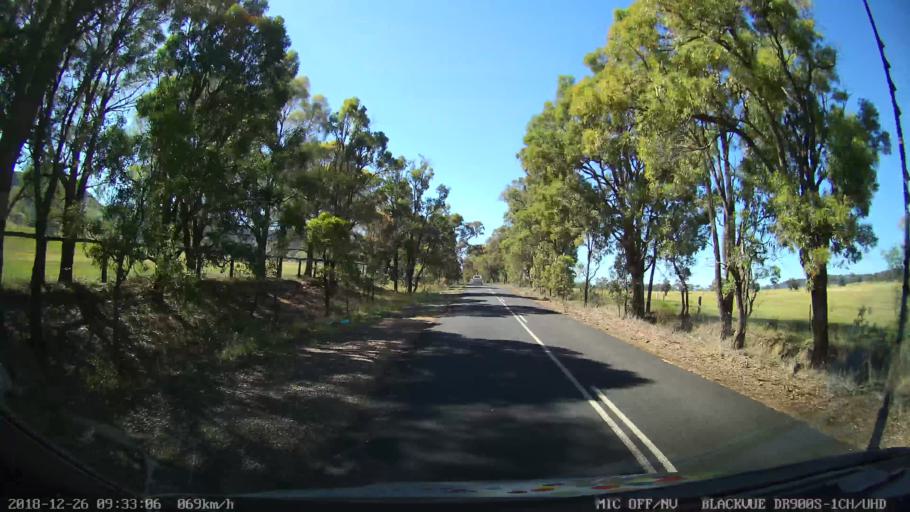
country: AU
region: New South Wales
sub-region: Mid-Western Regional
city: Kandos
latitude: -32.8913
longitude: 150.0338
